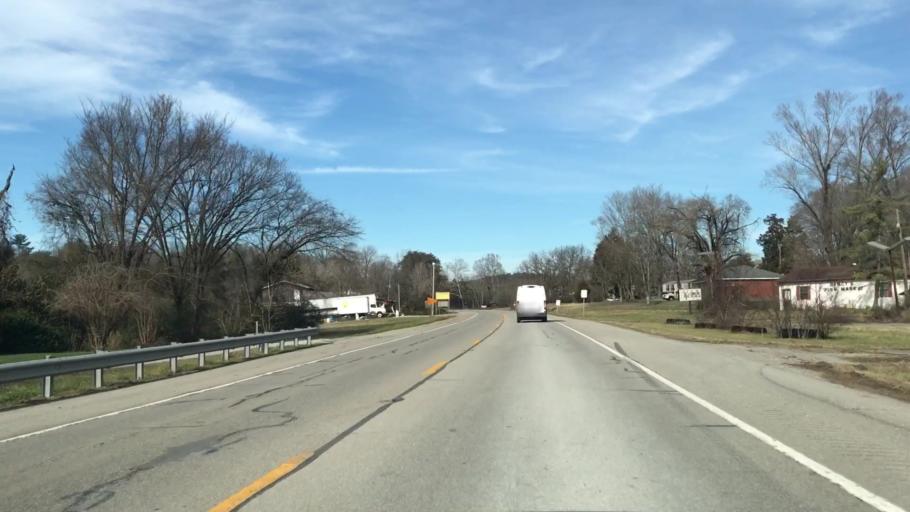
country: US
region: Kentucky
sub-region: Pulaski County
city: Somerset
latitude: 36.9594
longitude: -84.5825
